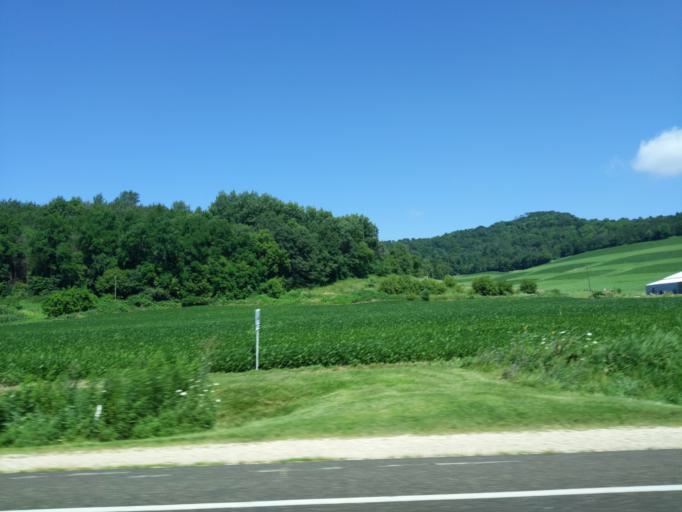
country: US
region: Wisconsin
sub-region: La Crosse County
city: La Crosse
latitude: 43.7614
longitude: -91.1832
